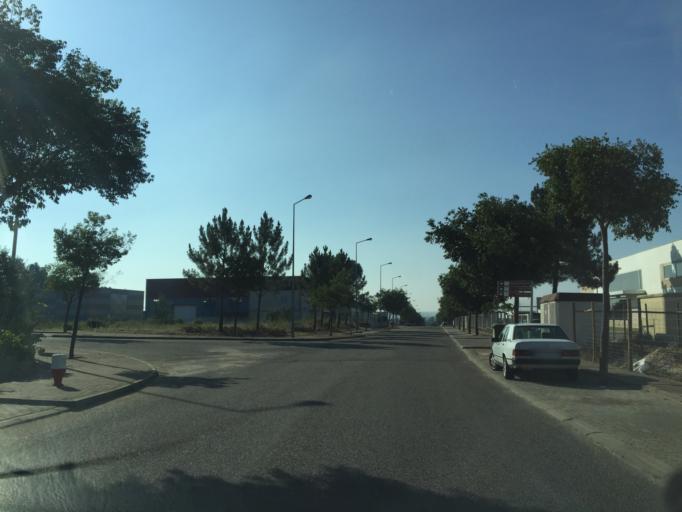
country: PT
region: Santarem
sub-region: Abrantes
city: Alferrarede
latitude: 39.4920
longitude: -8.1866
